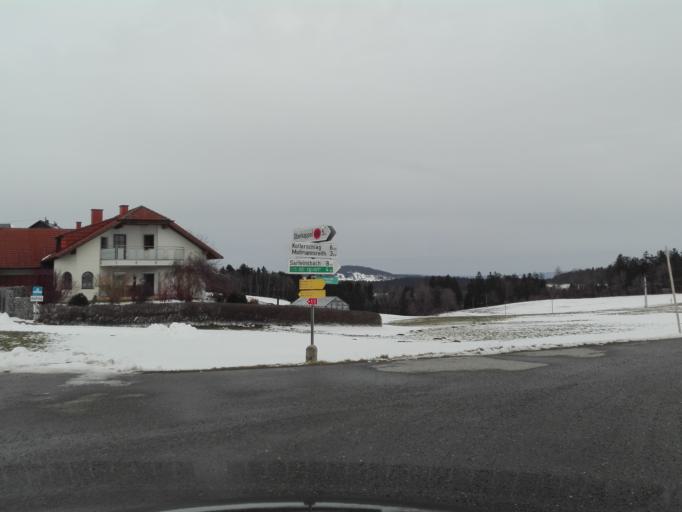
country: DE
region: Bavaria
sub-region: Lower Bavaria
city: Wegscheid
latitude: 48.5624
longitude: 13.8208
